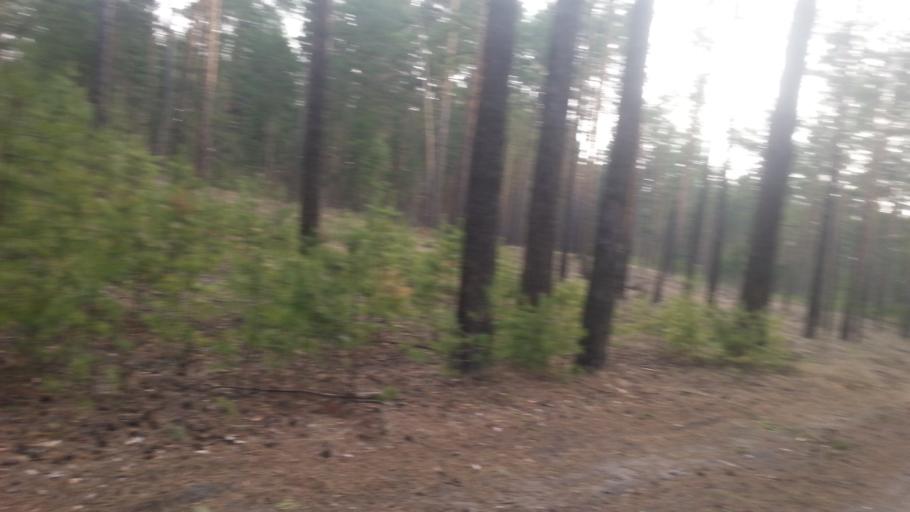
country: RU
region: Altai Krai
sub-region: Gorod Barnaulskiy
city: Barnaul
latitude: 53.3257
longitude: 83.7219
